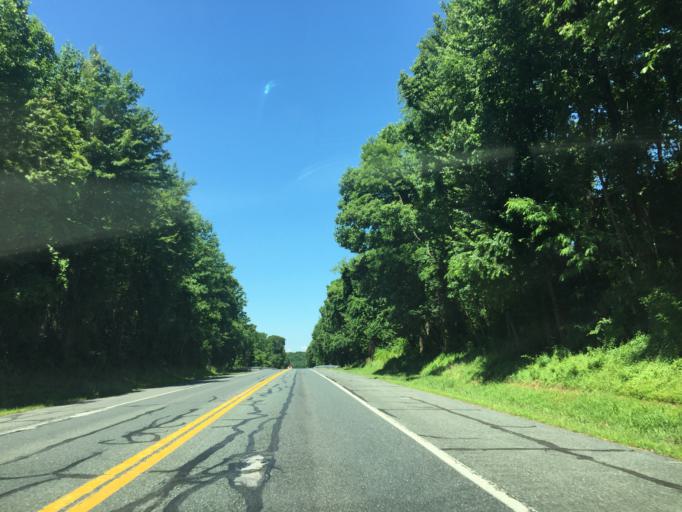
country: US
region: Maryland
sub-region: Harford County
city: Bel Air North
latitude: 39.5749
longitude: -76.4269
